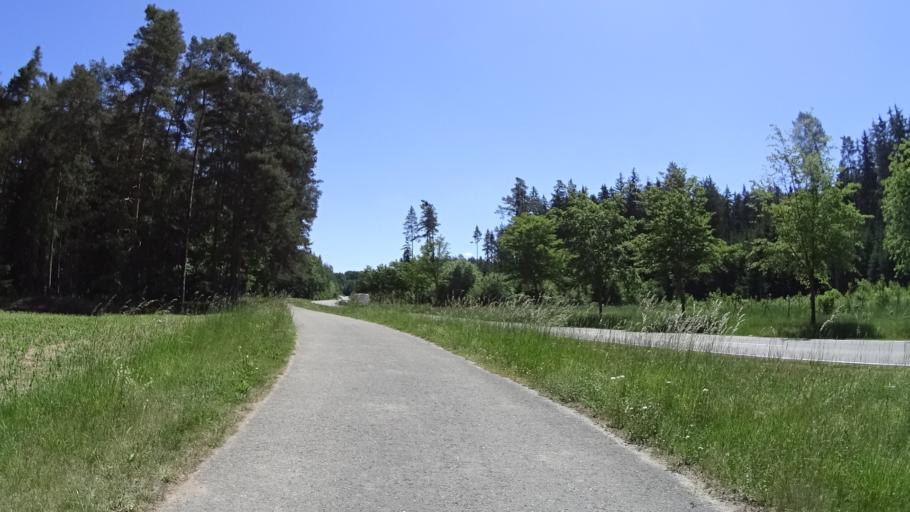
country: DE
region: Bavaria
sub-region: Regierungsbezirk Mittelfranken
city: Pleinfeld
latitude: 49.0984
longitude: 10.9621
